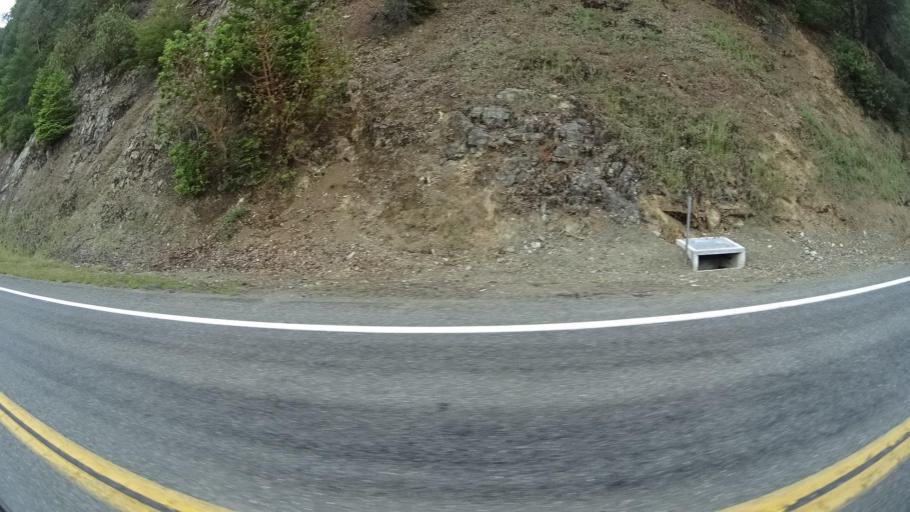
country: US
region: California
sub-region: Humboldt County
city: Willow Creek
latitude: 40.9980
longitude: -123.6267
